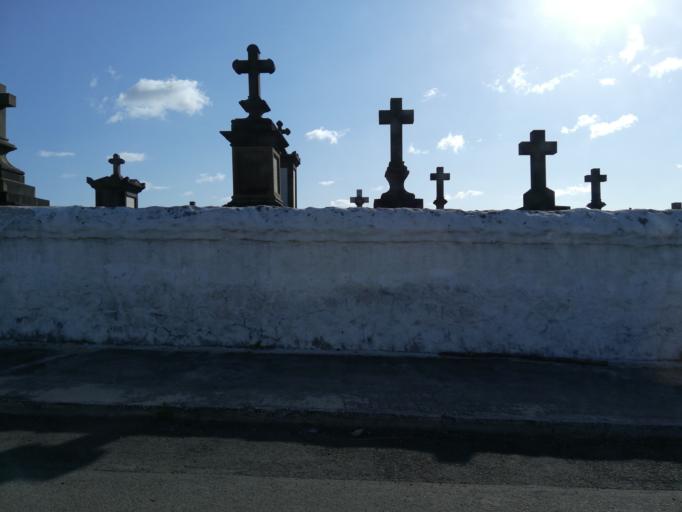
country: MU
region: Port Louis
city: Port Louis
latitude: -20.1609
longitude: 57.4871
